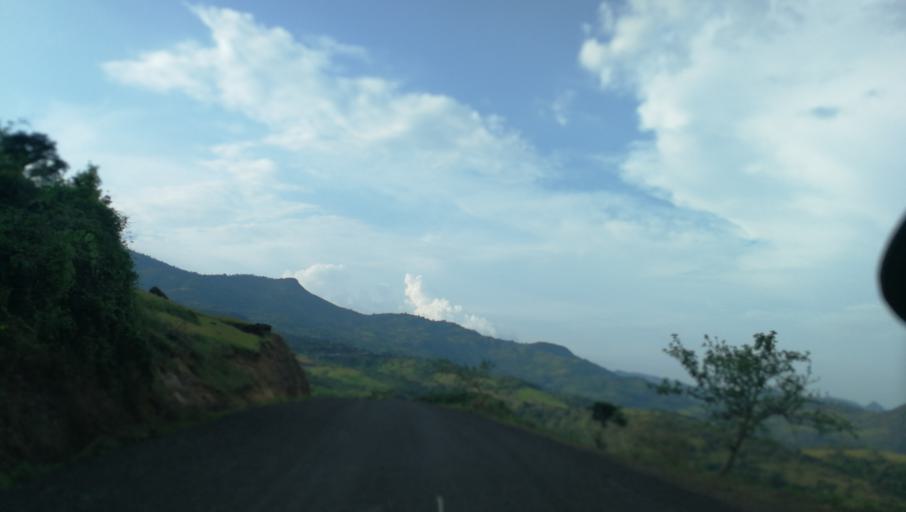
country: ET
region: Southern Nations, Nationalities, and People's Region
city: Areka
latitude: 6.8500
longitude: 37.2700
